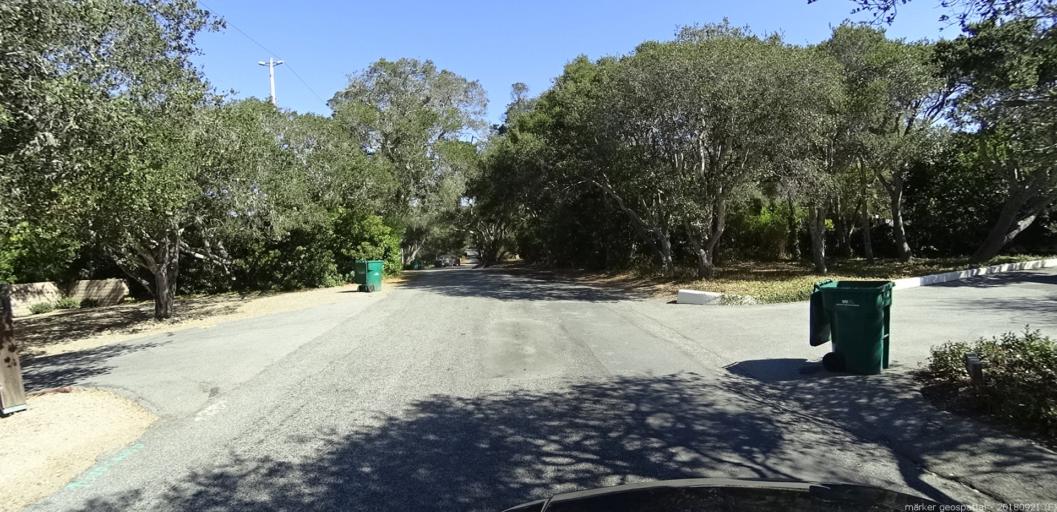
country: US
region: California
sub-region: Monterey County
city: Carmel-by-the-Sea
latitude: 36.5498
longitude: -121.9145
